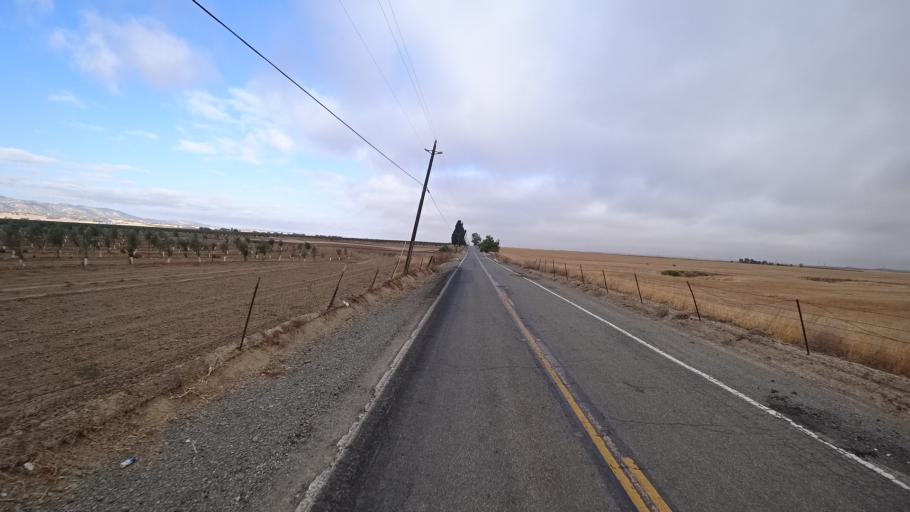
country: US
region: California
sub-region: Yolo County
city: Esparto
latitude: 38.7817
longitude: -122.0439
